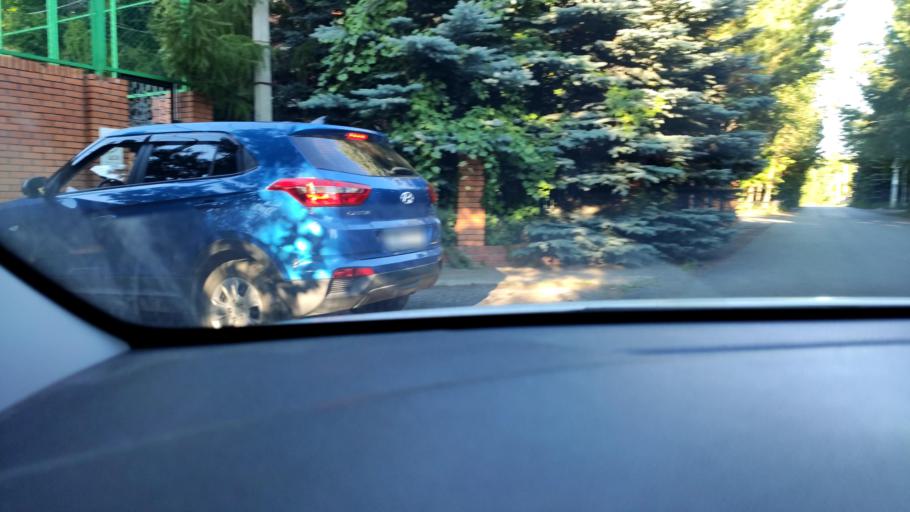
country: RU
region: Tatarstan
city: Vysokaya Gora
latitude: 55.8245
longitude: 49.2352
